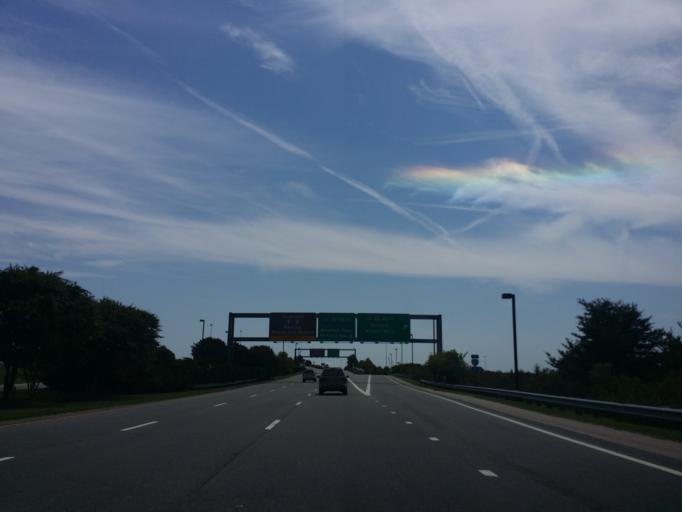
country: US
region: North Carolina
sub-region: Wake County
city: Morrisville
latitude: 35.8713
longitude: -78.8060
